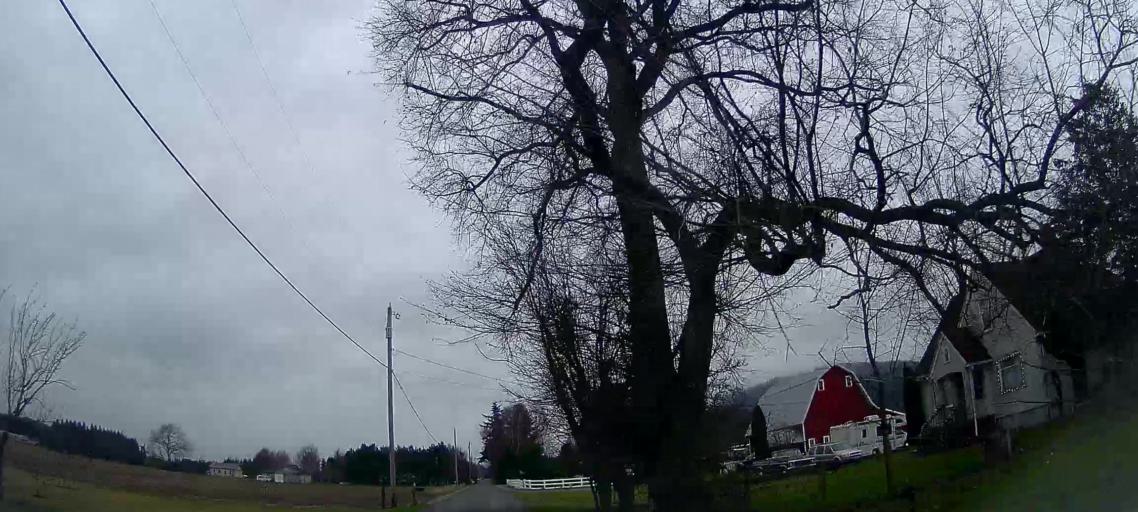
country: US
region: Washington
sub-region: Skagit County
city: Mount Vernon
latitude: 48.3747
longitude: -122.3242
